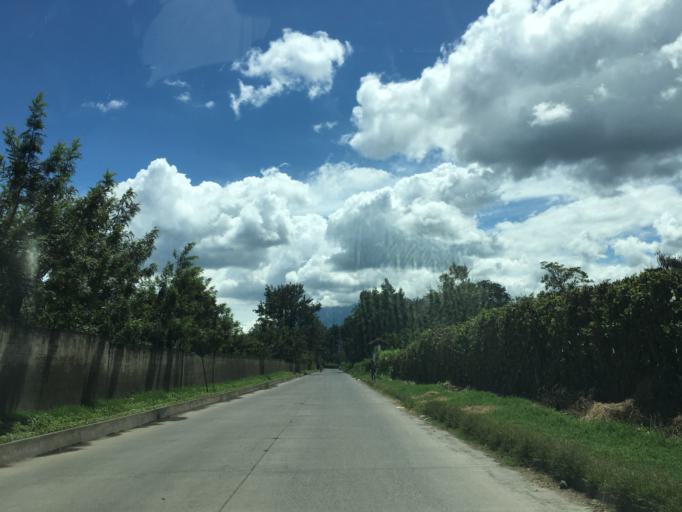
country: GT
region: Sacatepequez
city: Antigua Guatemala
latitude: 14.5445
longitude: -90.7329
